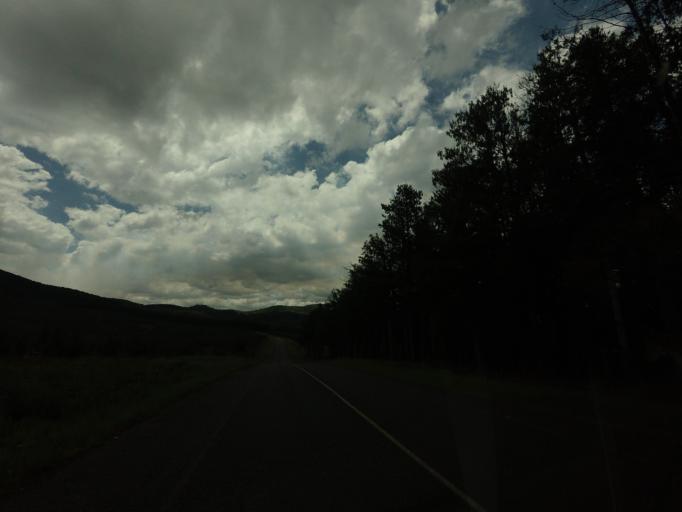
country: ZA
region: Mpumalanga
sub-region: Ehlanzeni District
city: Graksop
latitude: -24.9771
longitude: 30.8089
